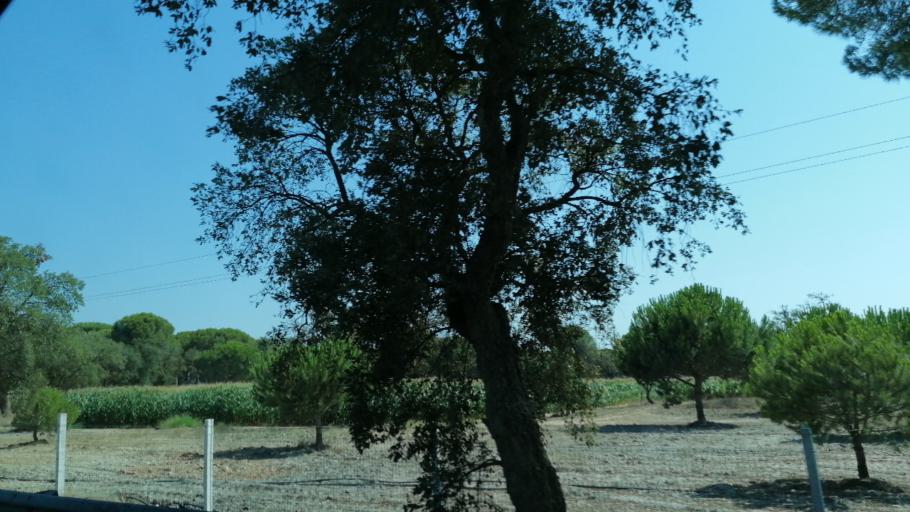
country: PT
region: Evora
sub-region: Vendas Novas
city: Vendas Novas
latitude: 38.7222
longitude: -8.6360
